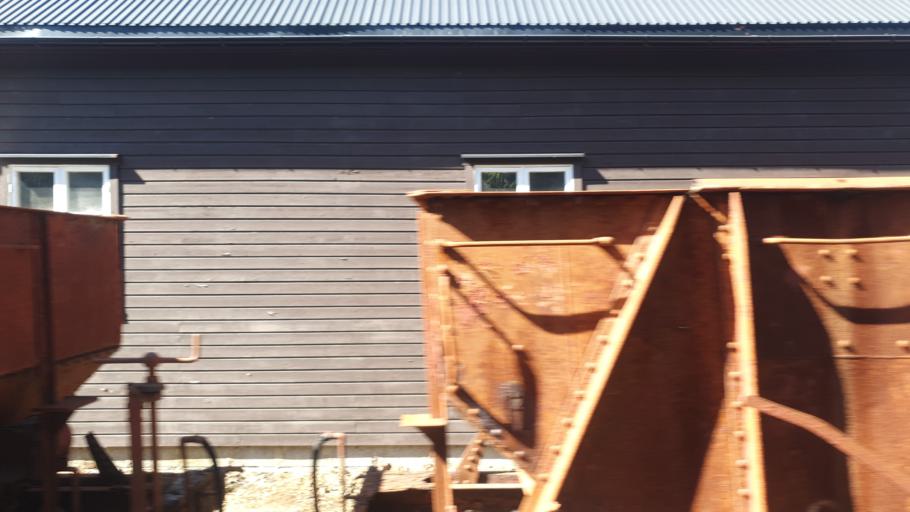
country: NO
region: Sor-Trondelag
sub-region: Meldal
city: Meldal
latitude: 63.1342
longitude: 9.7099
